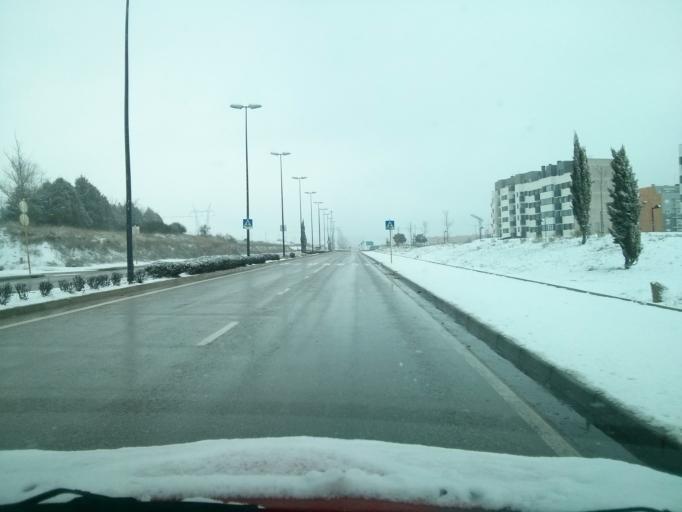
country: ES
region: Castille and Leon
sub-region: Provincia de Burgos
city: Burgos
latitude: 42.3655
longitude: -3.6750
